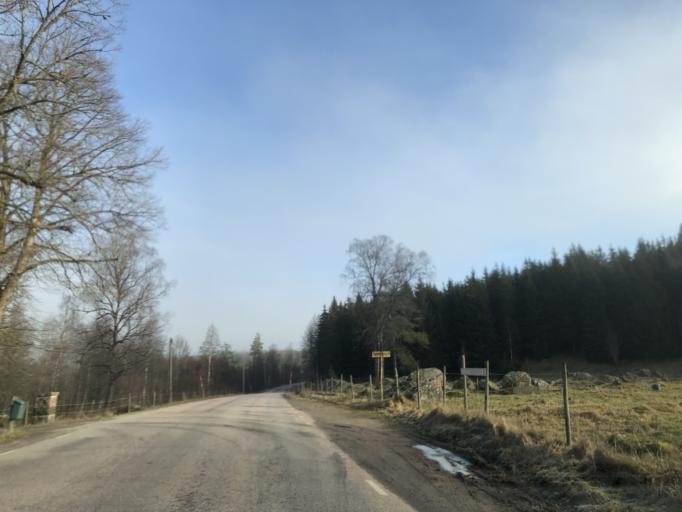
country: SE
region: Vaestra Goetaland
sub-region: Ulricehamns Kommun
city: Ulricehamn
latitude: 57.8284
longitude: 13.4565
